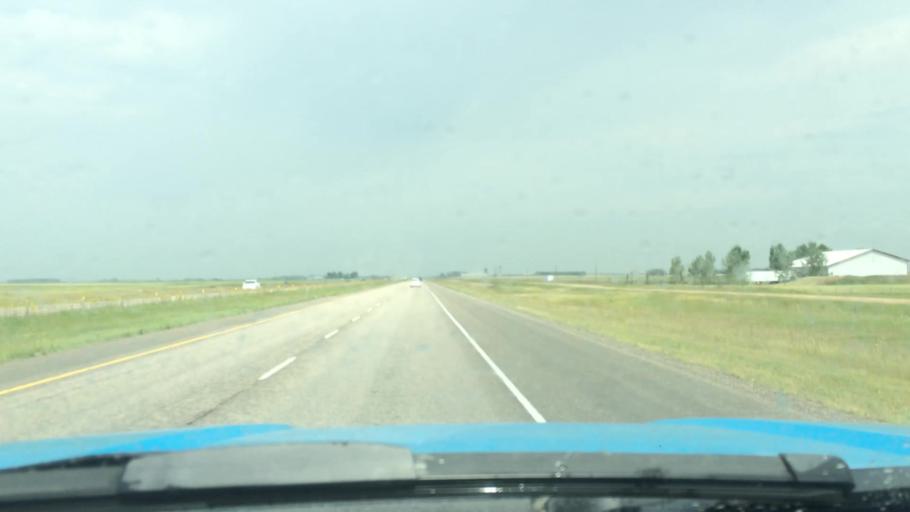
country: CA
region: Alberta
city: Olds
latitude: 51.6987
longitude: -114.0253
